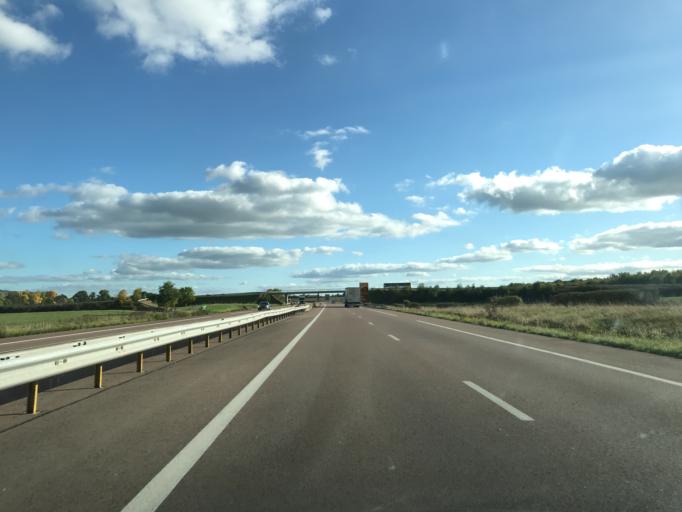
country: FR
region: Bourgogne
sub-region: Departement de la Cote-d'Or
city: Pouilly-en-Auxois
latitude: 47.2771
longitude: 4.5107
